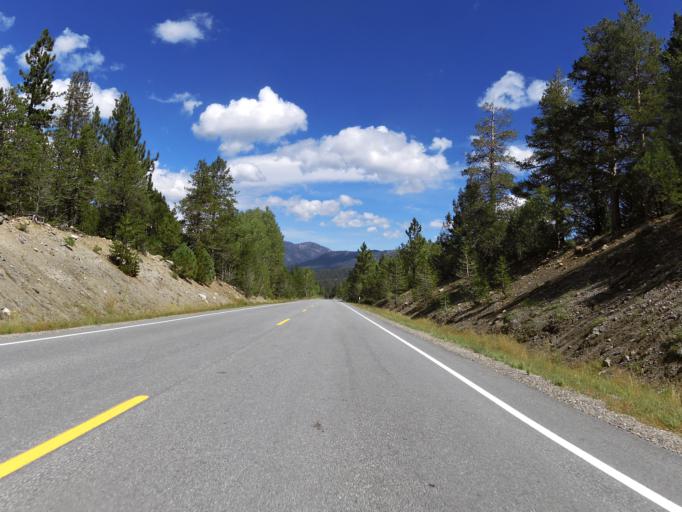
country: US
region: California
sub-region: El Dorado County
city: South Lake Tahoe
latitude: 38.7427
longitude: -119.9473
